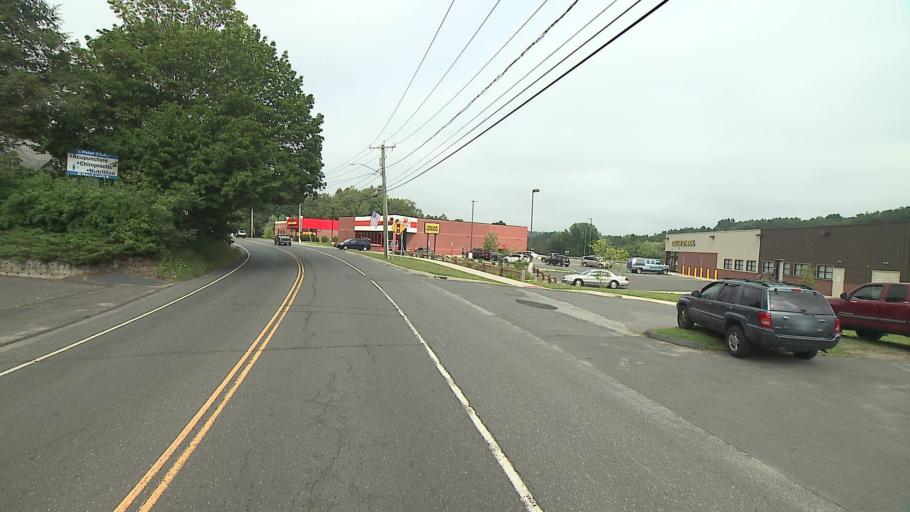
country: US
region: Connecticut
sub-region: Litchfield County
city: Oakville
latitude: 41.5905
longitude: -73.1029
